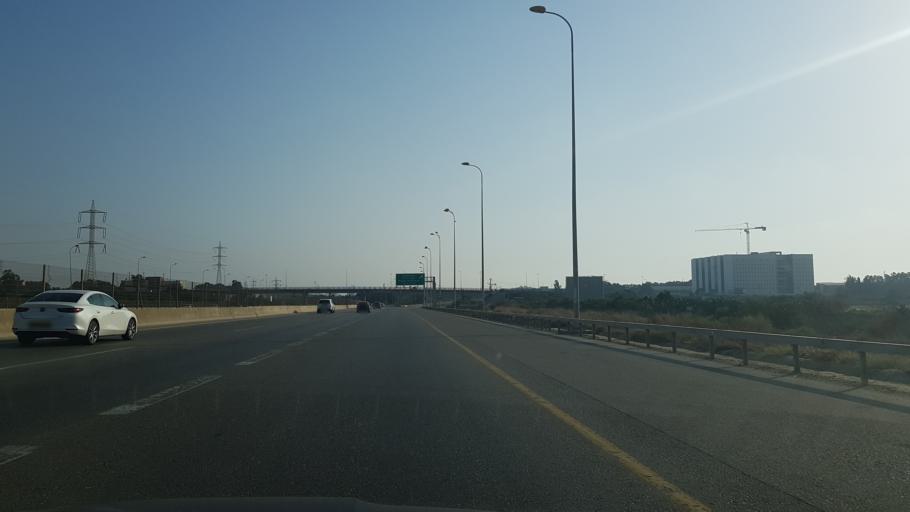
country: IL
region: Tel Aviv
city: Herzliyya
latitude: 32.1491
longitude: 34.8117
